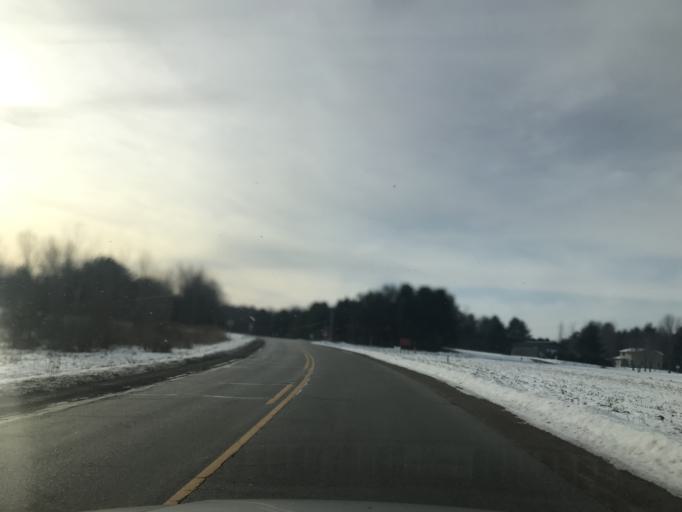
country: US
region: Wisconsin
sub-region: Brown County
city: Suamico
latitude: 44.6785
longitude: -88.0540
